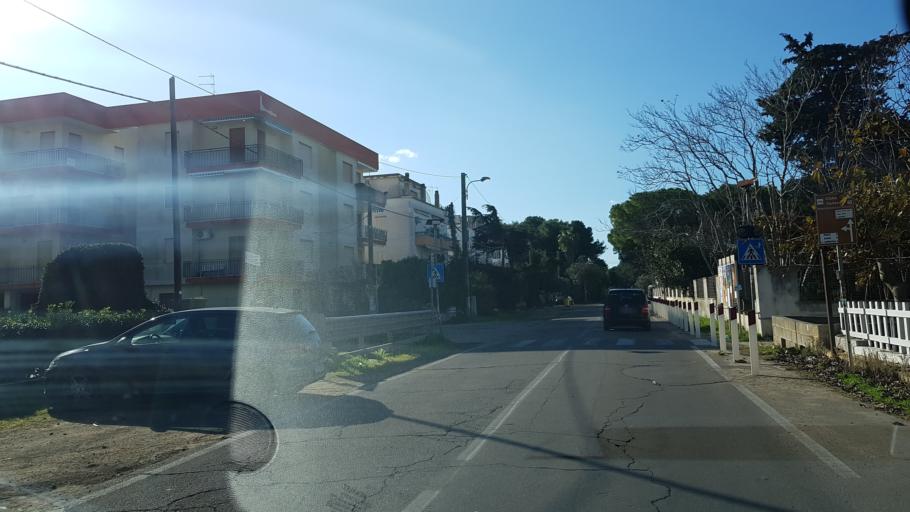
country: IT
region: Apulia
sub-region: Provincia di Lecce
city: Gallipoli
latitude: 40.0848
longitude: 18.0128
